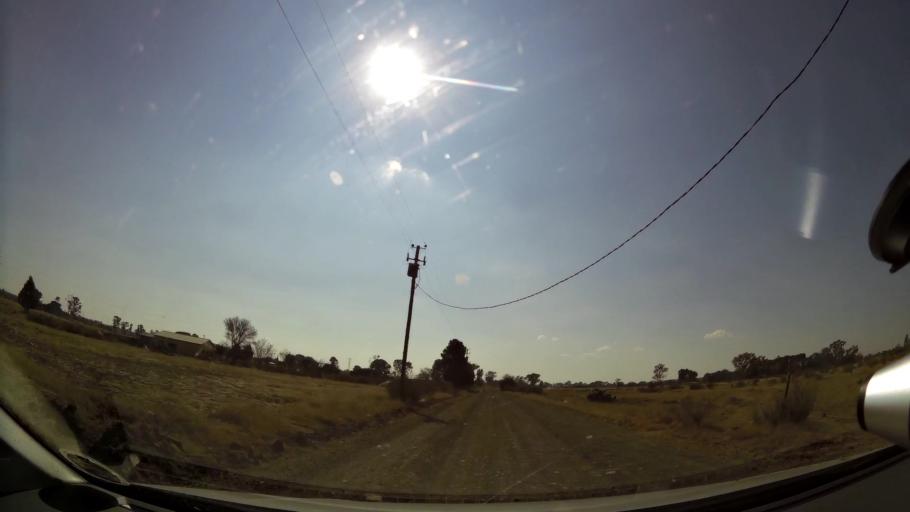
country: ZA
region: Orange Free State
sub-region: Mangaung Metropolitan Municipality
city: Bloemfontein
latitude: -29.1718
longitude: 26.3077
